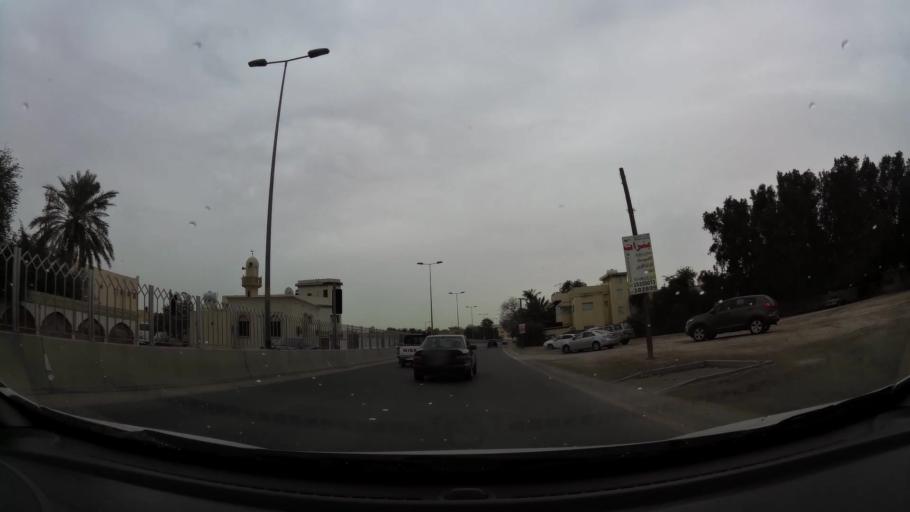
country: BH
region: Manama
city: Jidd Hafs
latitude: 26.2142
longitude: 50.5340
